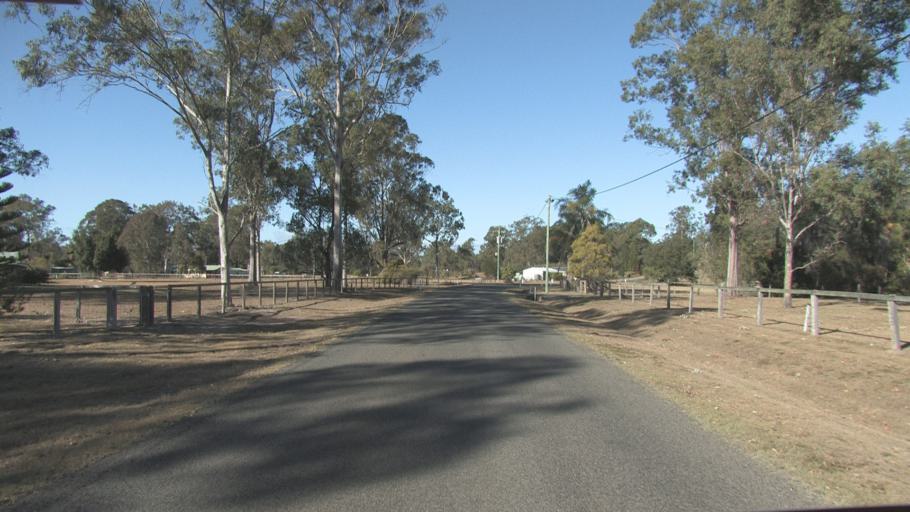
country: AU
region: Queensland
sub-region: Logan
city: North Maclean
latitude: -27.8288
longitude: 152.9901
